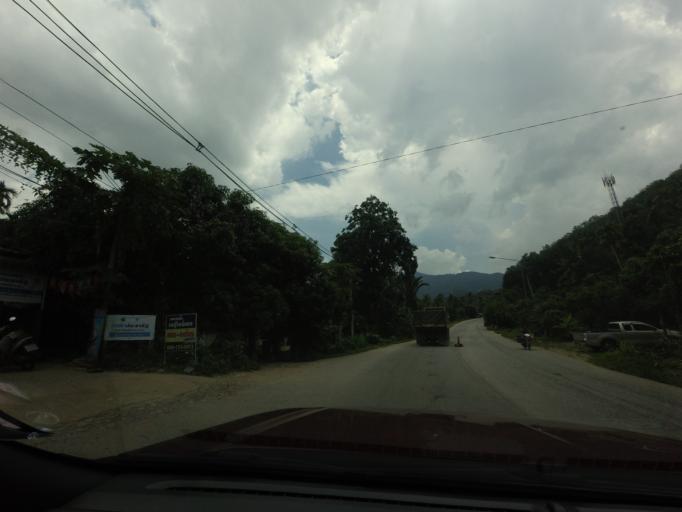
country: TH
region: Yala
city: Than To
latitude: 6.0712
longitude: 101.1951
